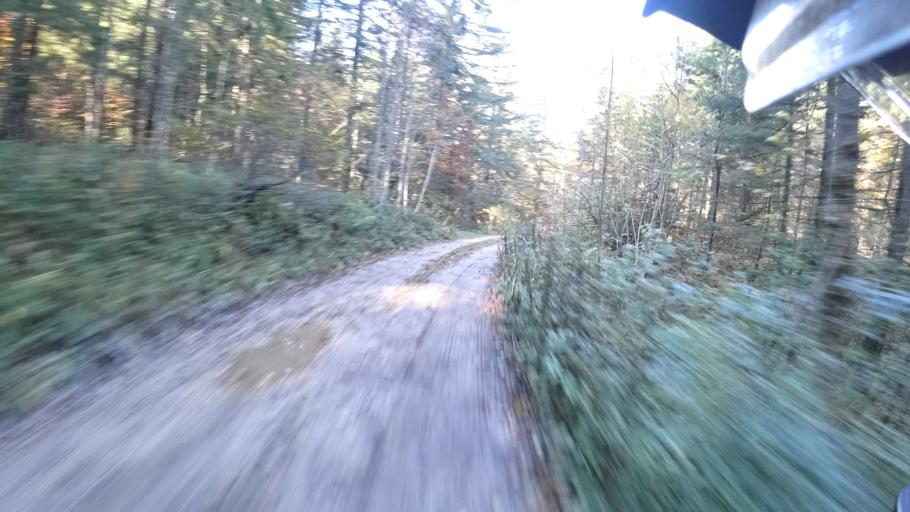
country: HR
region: Karlovacka
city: Plaski
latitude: 45.0284
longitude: 15.3617
